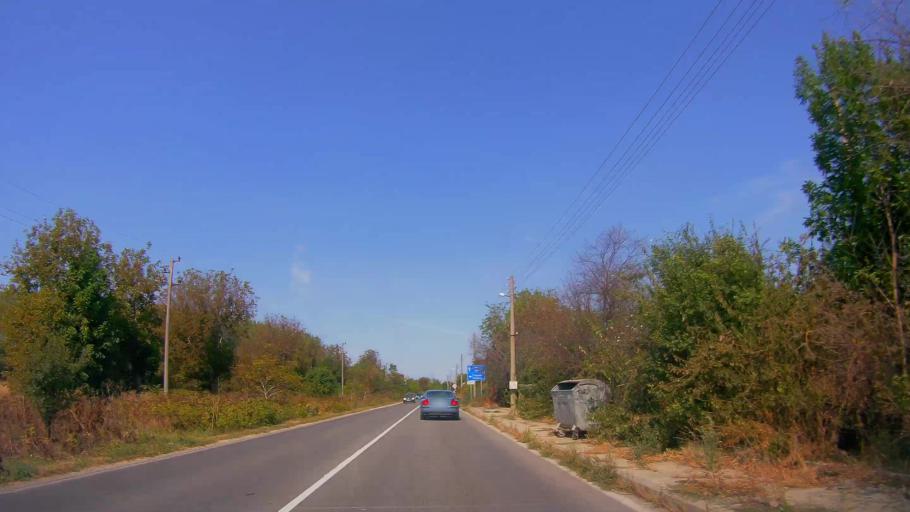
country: BG
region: Shumen
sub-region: Obshtina Smyadovo
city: Smyadovo
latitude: 43.1793
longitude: 27.0074
